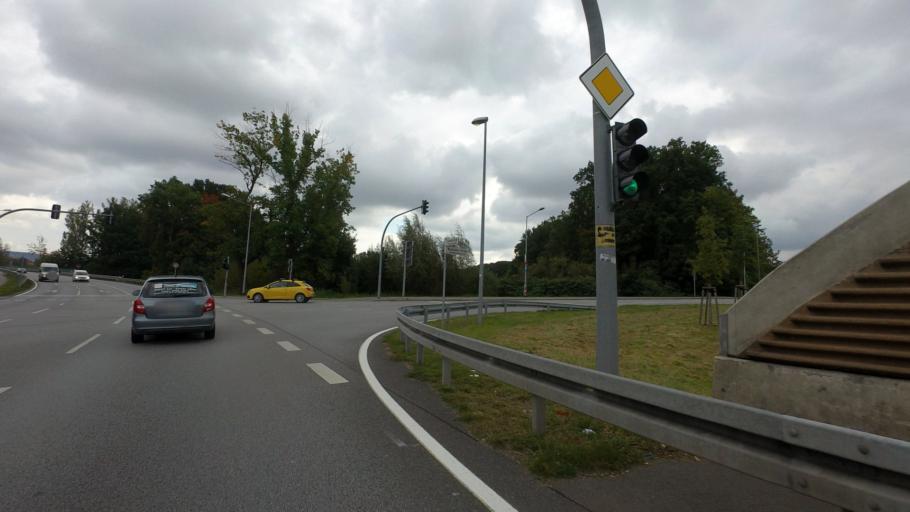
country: DE
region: Saxony
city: Bautzen
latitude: 51.1731
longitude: 14.4081
